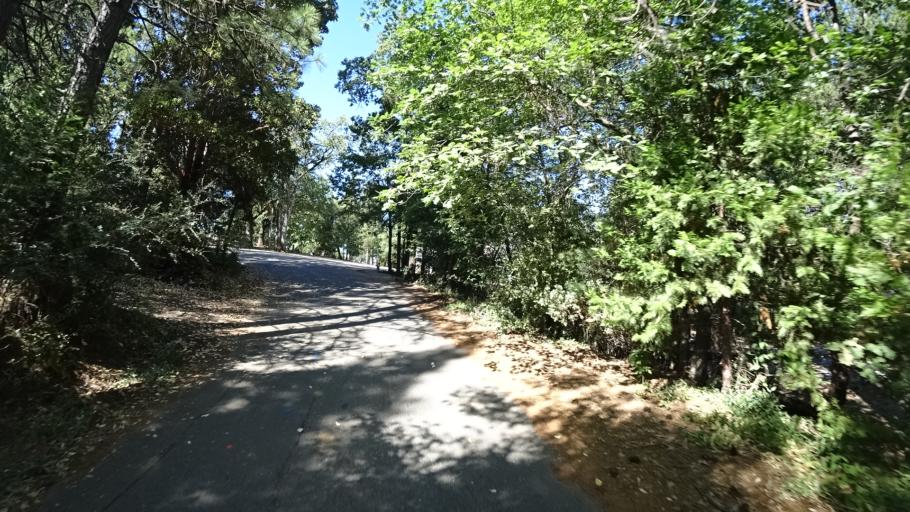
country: US
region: California
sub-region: Amador County
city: Pioneer
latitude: 38.4013
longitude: -120.5319
